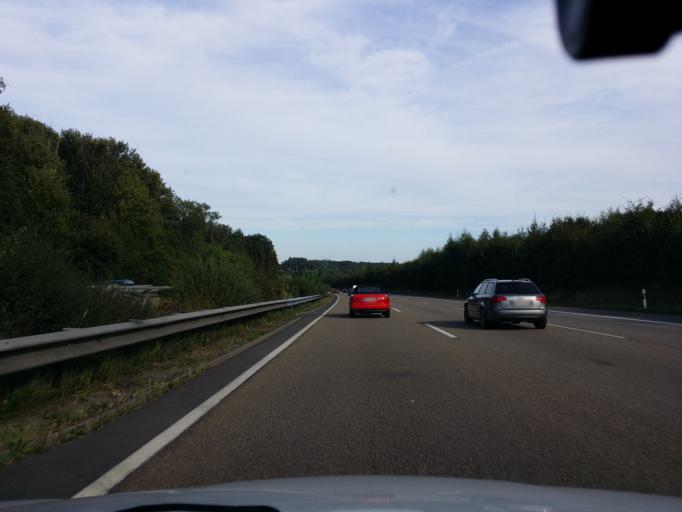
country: DE
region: Rheinland-Pfalz
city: Kleinmaischeid
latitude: 50.5242
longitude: 7.6206
